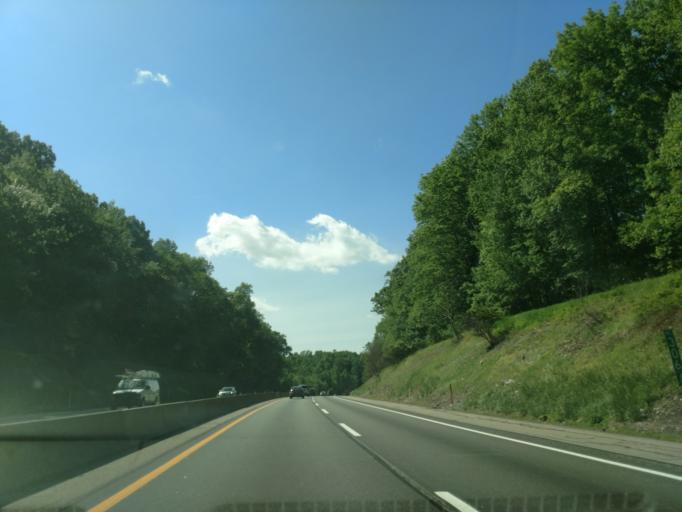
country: US
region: Pennsylvania
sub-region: Chester County
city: Elverson
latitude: 40.1011
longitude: -75.7525
